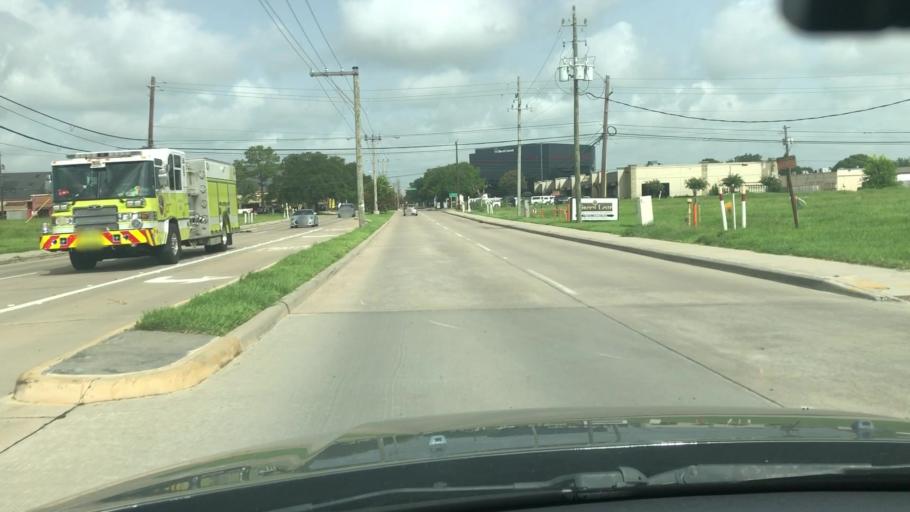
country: US
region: Texas
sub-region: Harris County
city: Webster
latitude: 29.5506
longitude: -95.1121
